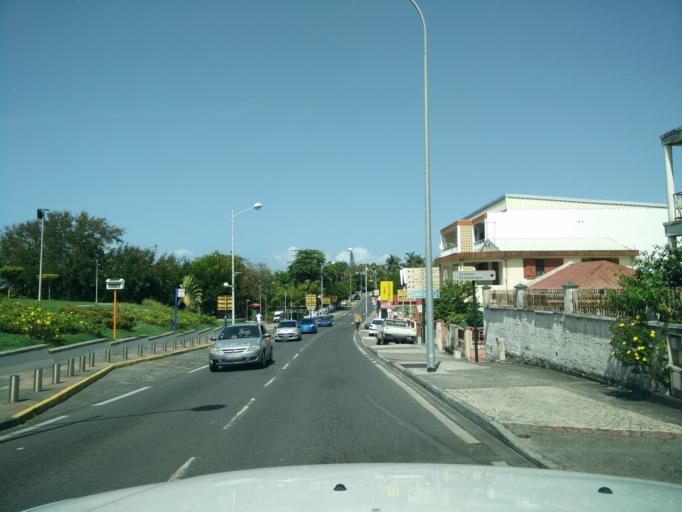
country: GP
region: Guadeloupe
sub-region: Guadeloupe
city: Le Gosier
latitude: 16.2061
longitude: -61.4960
